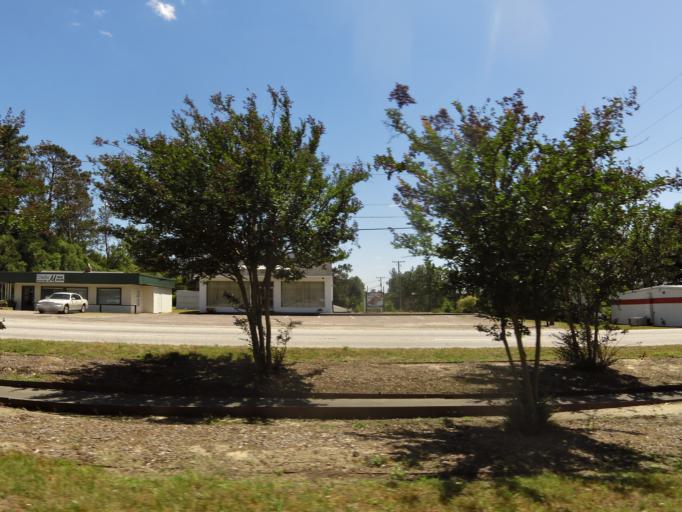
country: US
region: South Carolina
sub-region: Aiken County
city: Warrenville
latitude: 33.5629
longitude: -81.7716
